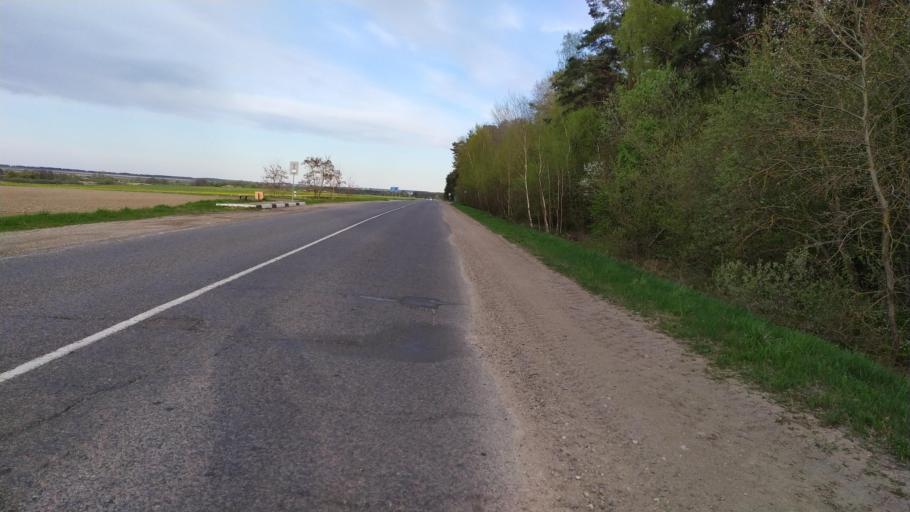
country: BY
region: Brest
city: Kamyanyets
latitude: 52.4169
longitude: 23.7003
